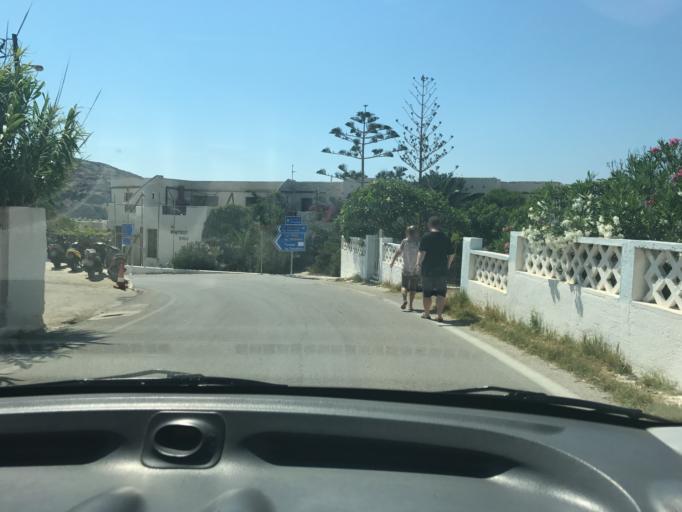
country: GR
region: South Aegean
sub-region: Nomos Dodekanisou
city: Karpathos
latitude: 35.4759
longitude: 27.1188
